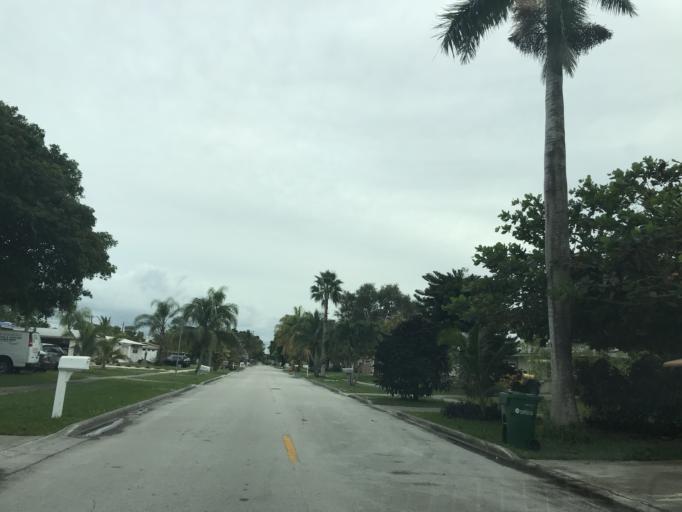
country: US
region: Florida
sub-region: Broward County
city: Margate
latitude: 26.2475
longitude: -80.2028
